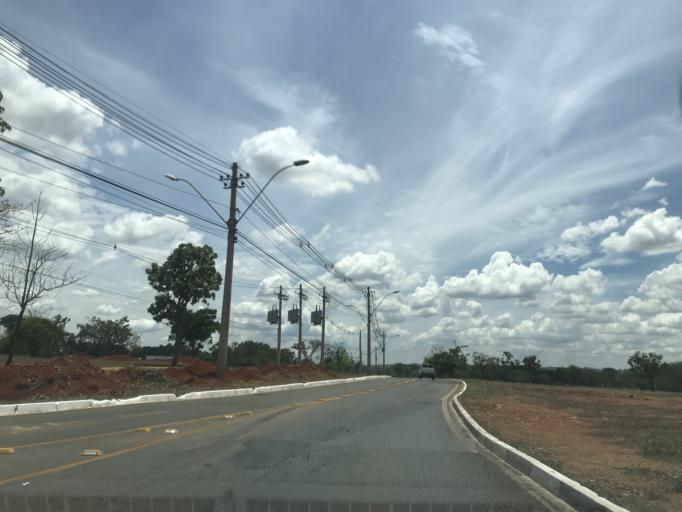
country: BR
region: Federal District
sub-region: Brasilia
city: Brasilia
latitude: -15.8658
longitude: -47.9370
